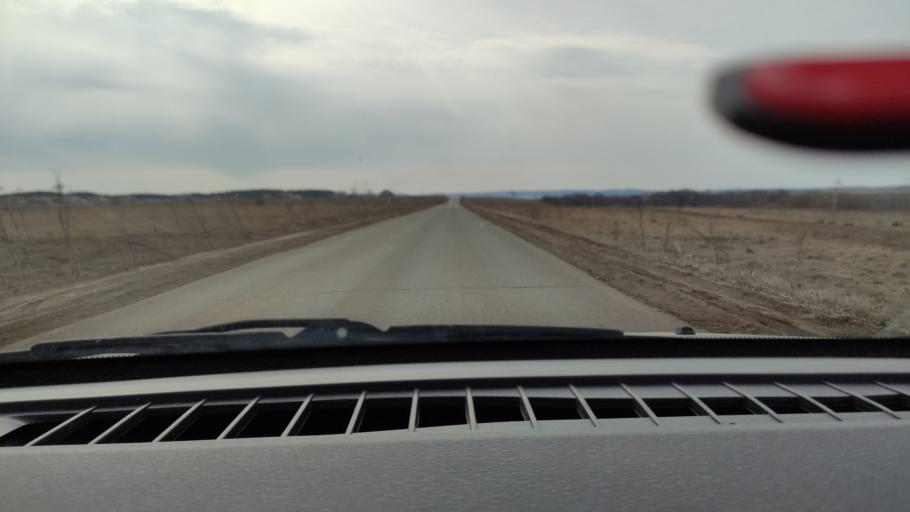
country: RU
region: Perm
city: Kultayevo
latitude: 57.9049
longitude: 55.9917
